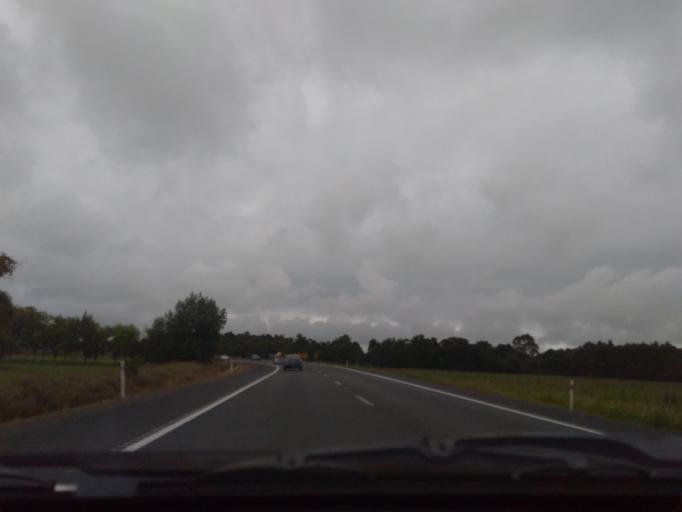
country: NZ
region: Northland
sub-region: Whangarei
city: Ruakaka
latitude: -35.8606
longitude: 174.3913
